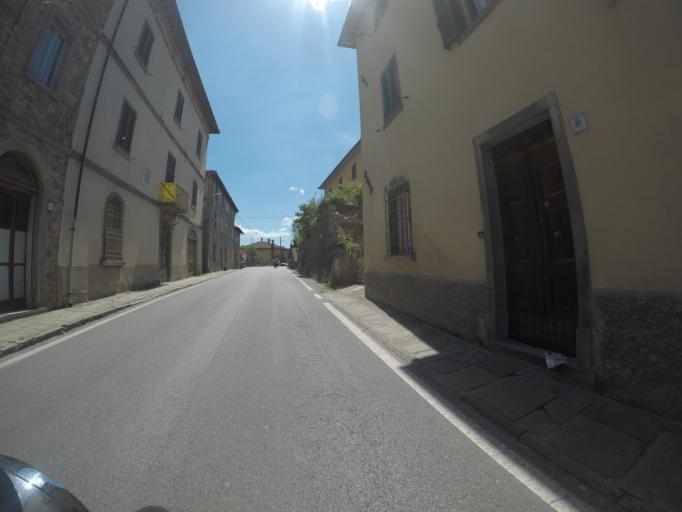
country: IT
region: Tuscany
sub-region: Provincia di Lucca
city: Villa Collemandina
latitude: 44.1339
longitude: 10.3718
